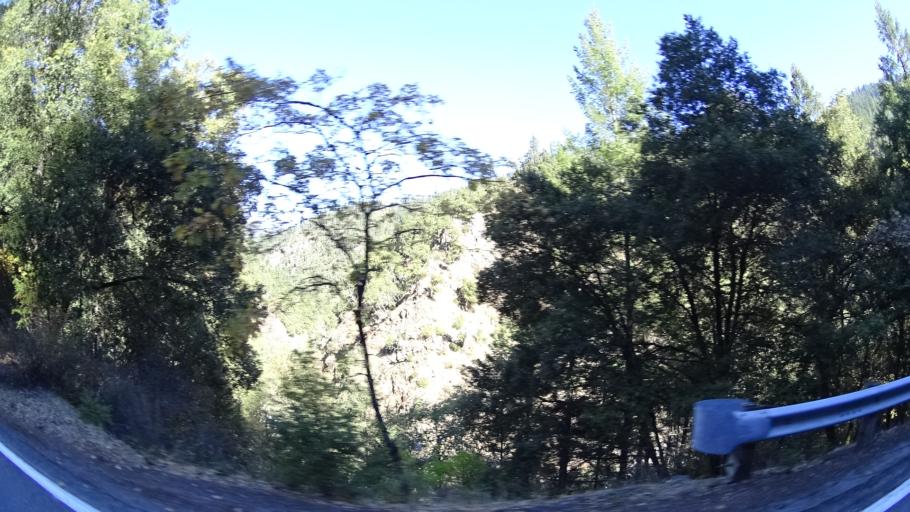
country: US
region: California
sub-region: Siskiyou County
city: Happy Camp
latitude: 41.3613
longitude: -123.4140
